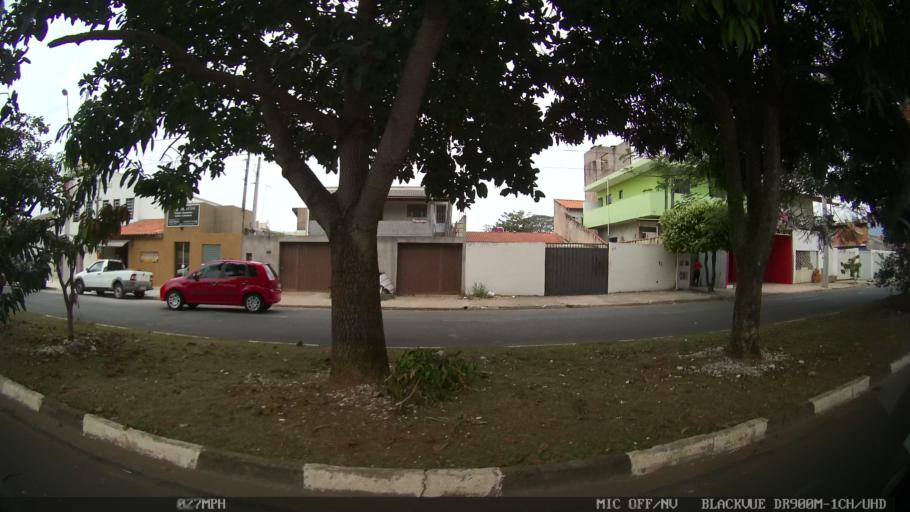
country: BR
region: Sao Paulo
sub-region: Paulinia
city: Paulinia
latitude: -22.7188
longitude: -47.1710
